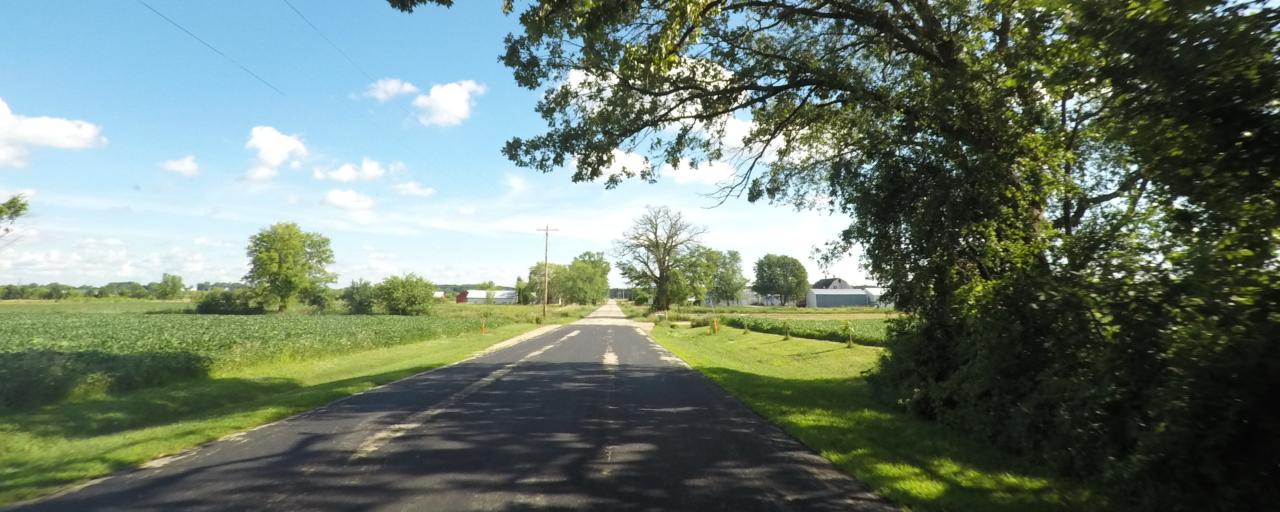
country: US
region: Wisconsin
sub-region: Rock County
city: Edgerton
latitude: 42.8478
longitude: -89.1320
